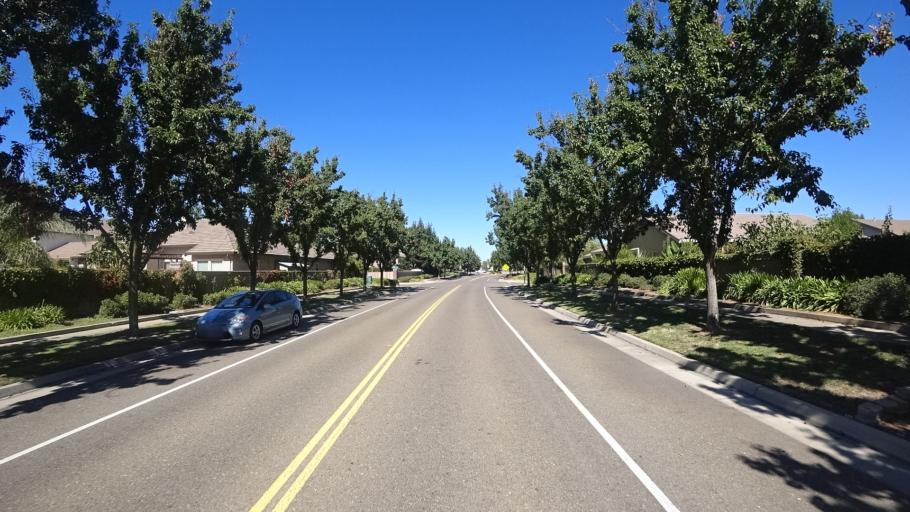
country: US
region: California
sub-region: Sacramento County
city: Elk Grove
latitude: 38.4073
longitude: -121.3390
